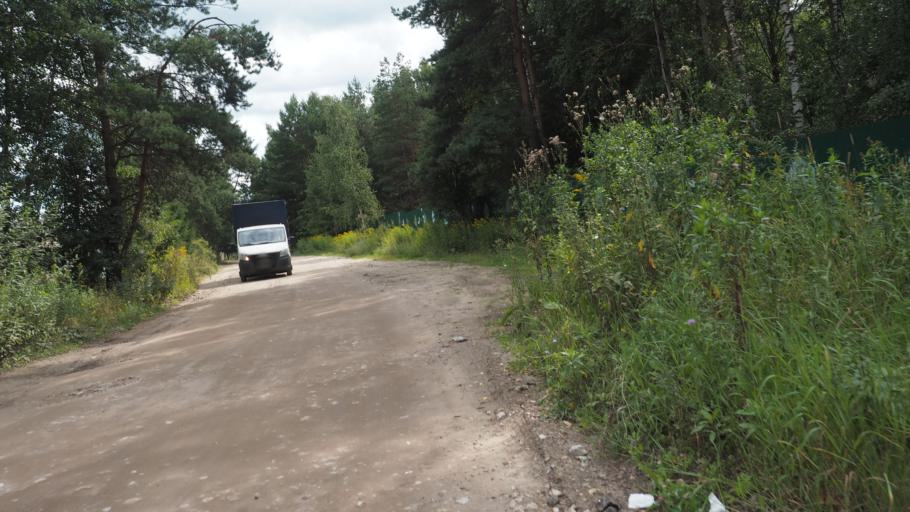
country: RU
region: Moskovskaya
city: Ramenskoye
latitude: 55.5742
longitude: 38.2704
